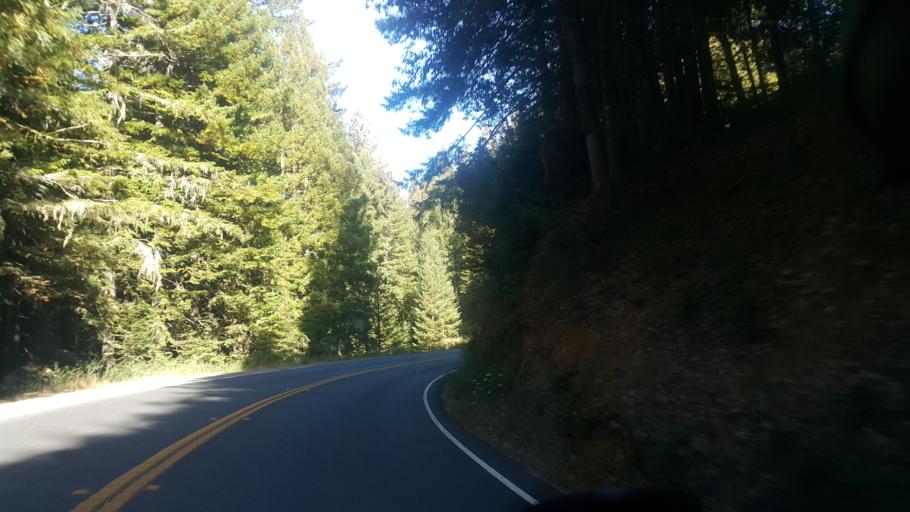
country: US
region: California
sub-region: Mendocino County
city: Fort Bragg
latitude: 39.3639
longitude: -123.6710
